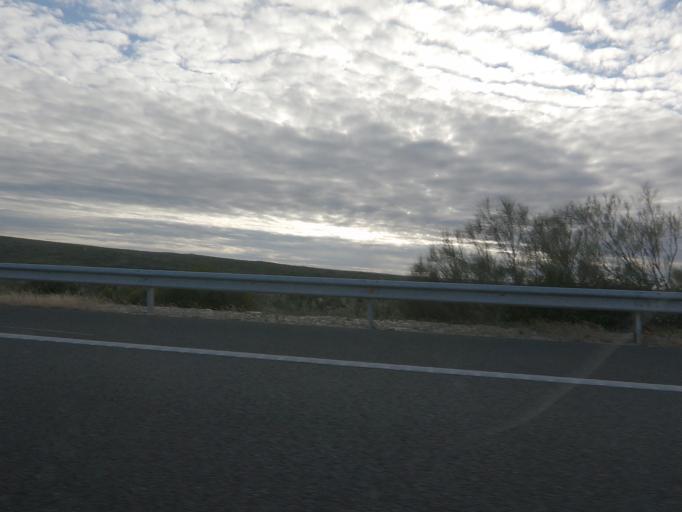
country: ES
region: Extremadura
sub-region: Provincia de Caceres
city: Hinojal
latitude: 39.6778
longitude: -6.3989
